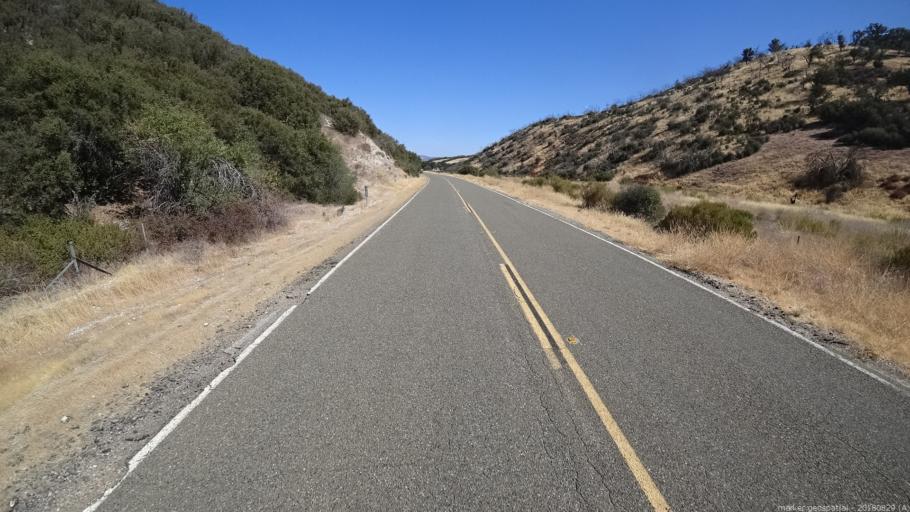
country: US
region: California
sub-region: San Luis Obispo County
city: Lake Nacimiento
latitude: 35.8640
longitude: -121.0623
